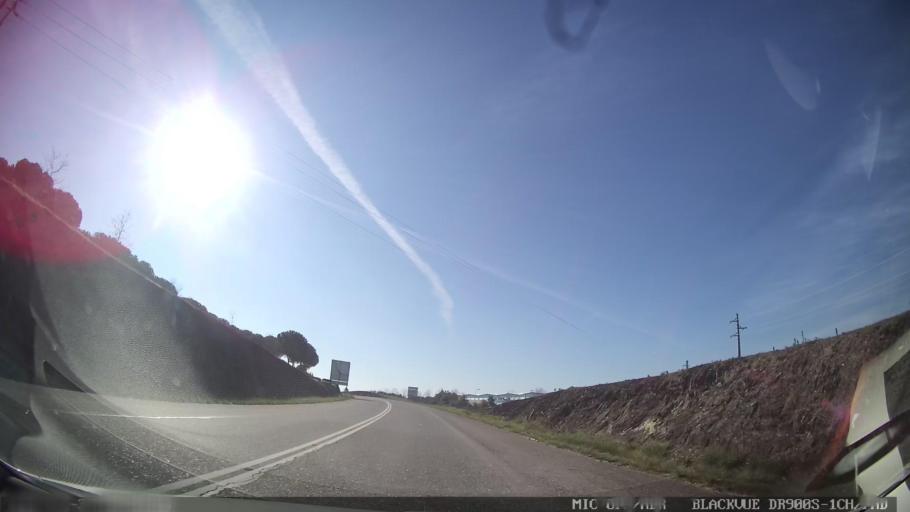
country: PT
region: Castelo Branco
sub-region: Castelo Branco
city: Castelo Branco
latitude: 39.8222
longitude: -7.5179
